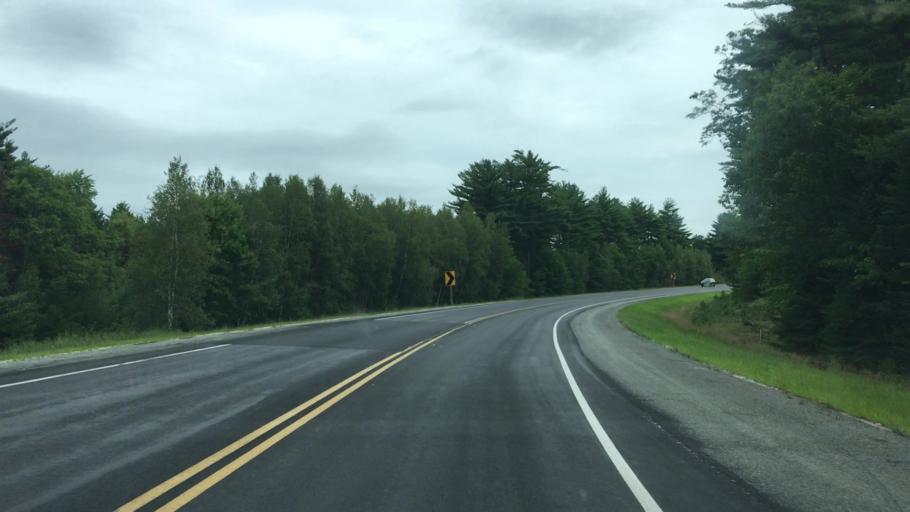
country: US
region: Maine
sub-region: Washington County
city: Cherryfield
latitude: 44.9091
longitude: -67.8566
